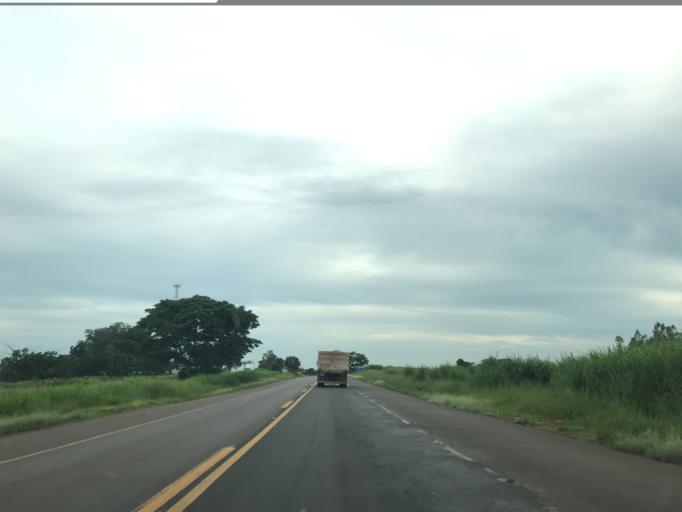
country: BR
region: Sao Paulo
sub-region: Tupa
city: Tupa
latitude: -21.6565
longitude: -50.5372
